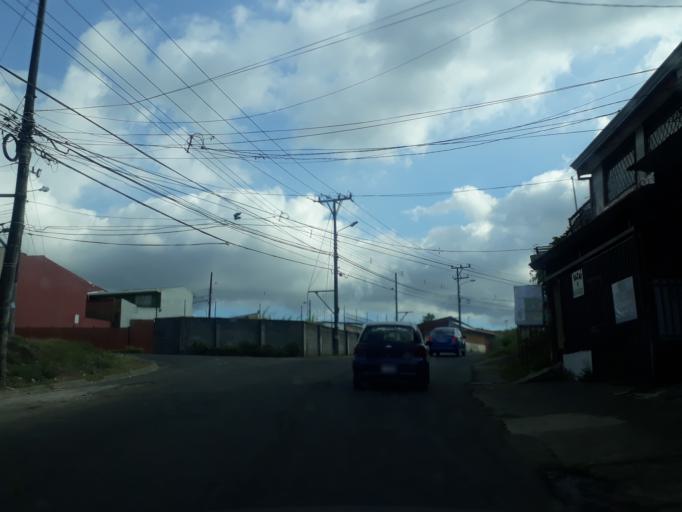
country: CR
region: San Jose
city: Ipis
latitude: 9.9887
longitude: -84.0256
